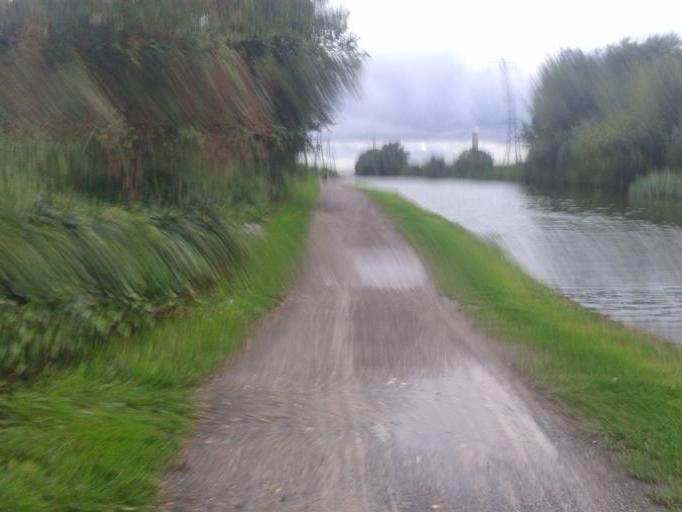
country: GB
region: England
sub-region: Greater London
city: Walthamstow
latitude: 51.6248
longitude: -0.0328
